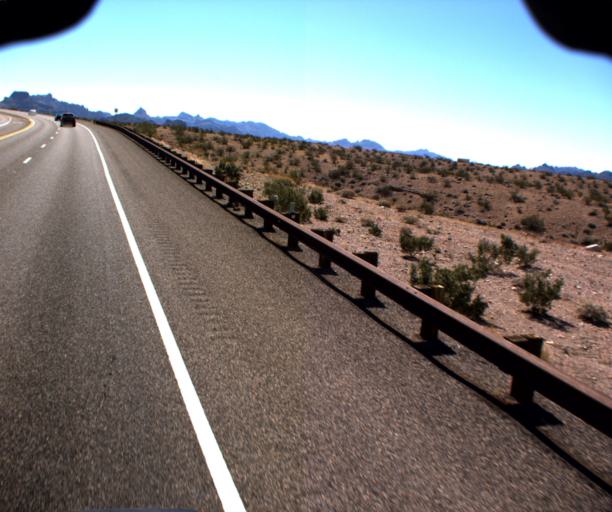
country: US
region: Nevada
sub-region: Clark County
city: Laughlin
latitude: 35.1853
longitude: -114.4999
